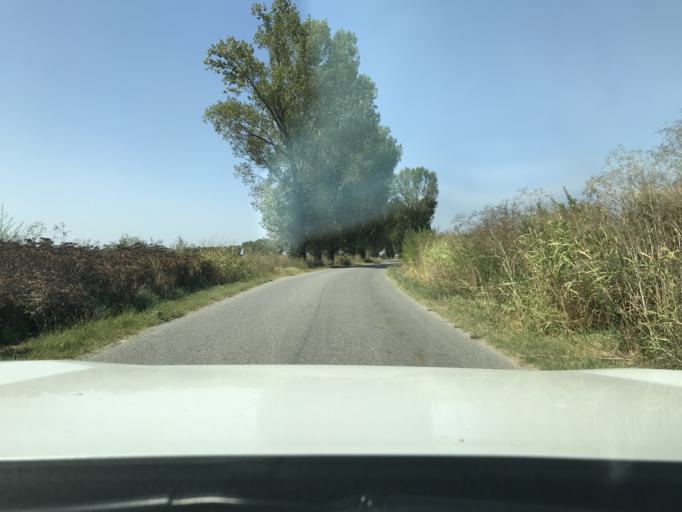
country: RO
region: Olt
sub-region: Comuna Falcoiu
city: Falcoiu
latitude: 44.2355
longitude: 24.3617
